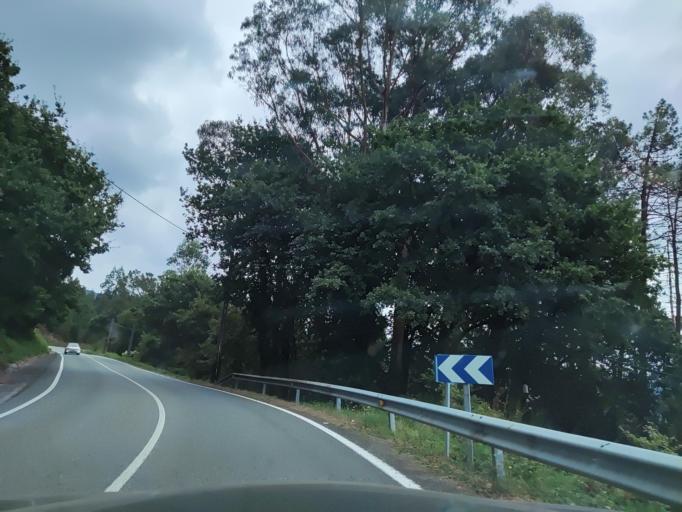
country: ES
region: Galicia
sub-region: Provincia da Coruna
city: Padron
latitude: 42.7393
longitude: -8.6311
